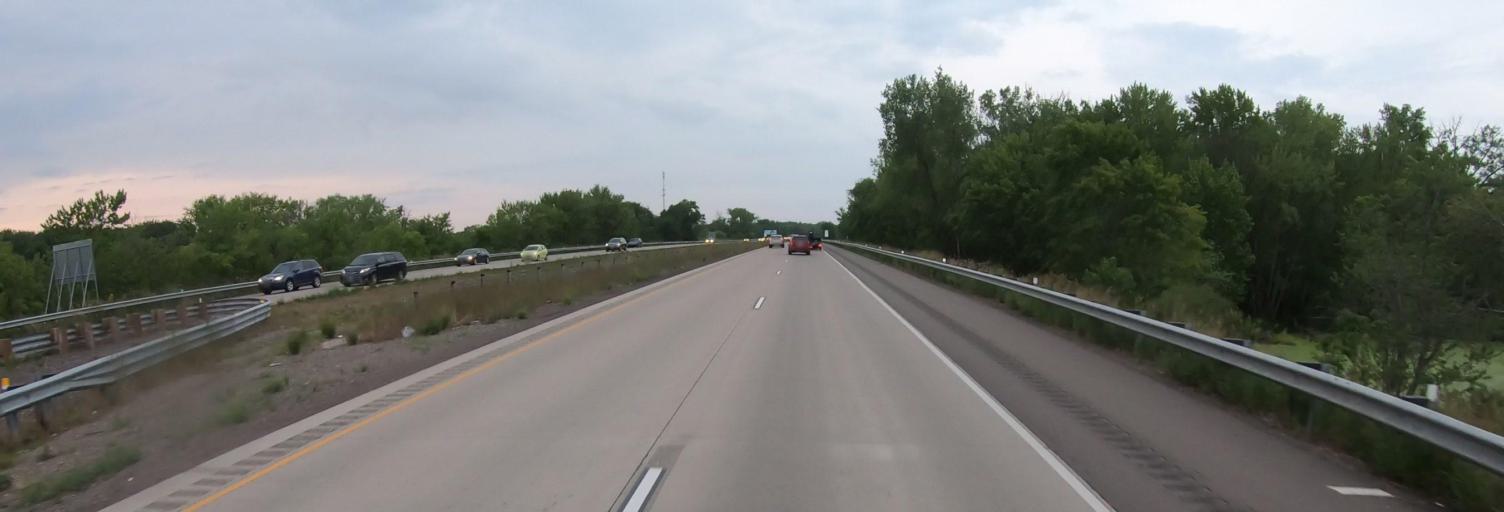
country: US
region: Minnesota
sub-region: Pine County
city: Pine City
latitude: 45.8306
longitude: -92.9827
